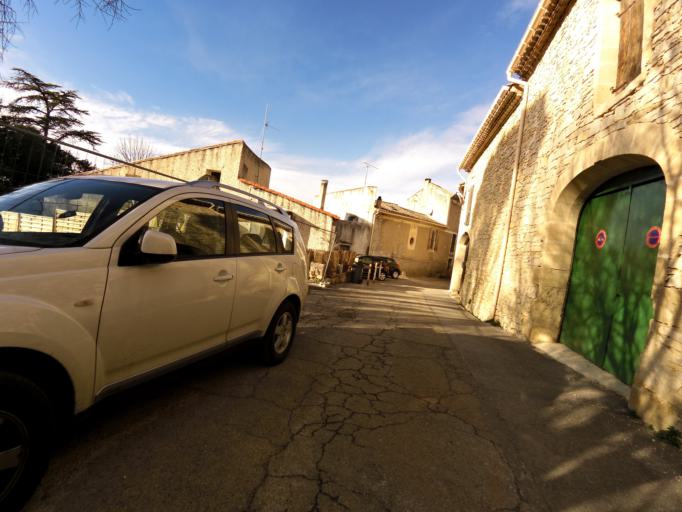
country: FR
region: Languedoc-Roussillon
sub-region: Departement du Gard
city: Langlade
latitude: 43.8026
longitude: 4.2482
